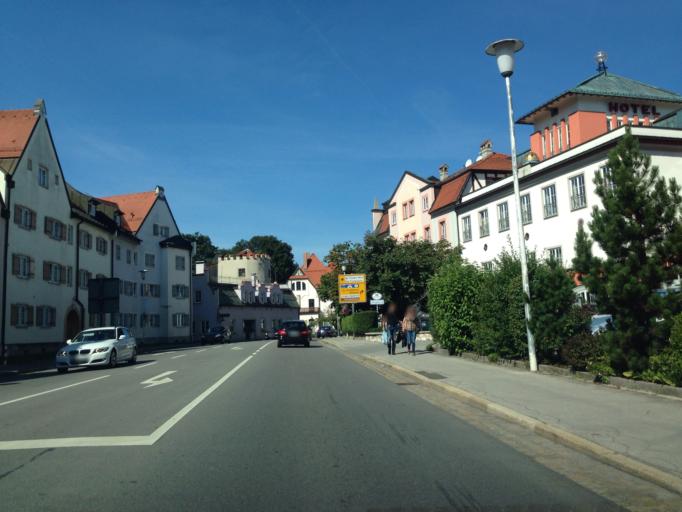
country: DE
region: Bavaria
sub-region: Swabia
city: Fuessen
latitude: 47.5688
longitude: 10.7029
